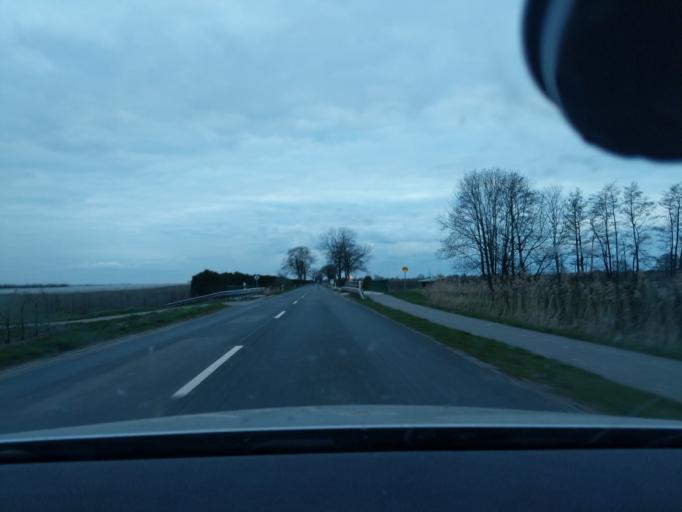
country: DE
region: Lower Saxony
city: Neu Wulmstorf
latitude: 53.5230
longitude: 9.7588
